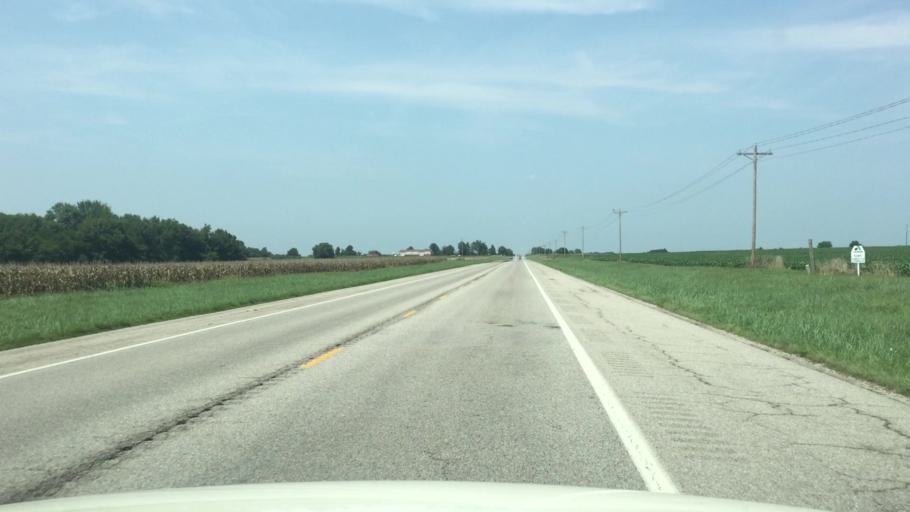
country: US
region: Kansas
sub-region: Crawford County
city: Pittsburg
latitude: 37.2631
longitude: -94.7052
